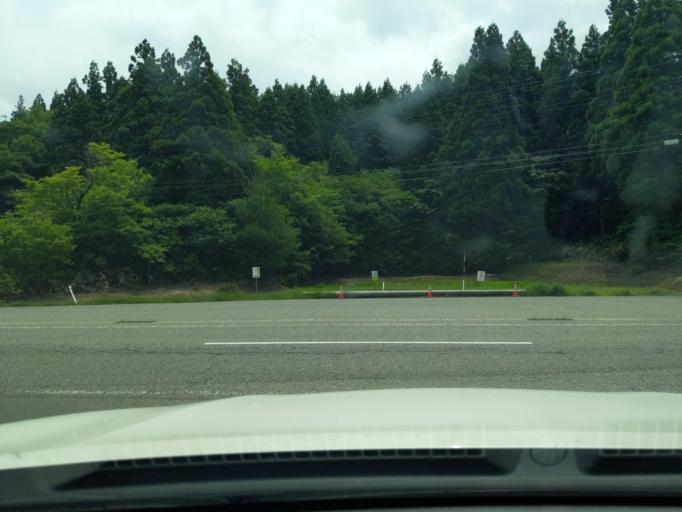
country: JP
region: Niigata
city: Kashiwazaki
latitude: 37.3327
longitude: 138.5912
